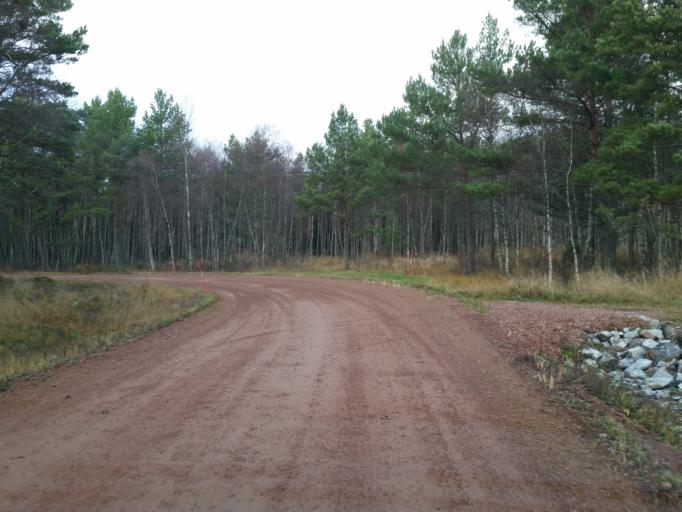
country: AX
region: Alands skaergard
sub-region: Kumlinge
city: Kumlinge
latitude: 60.2682
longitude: 20.8131
